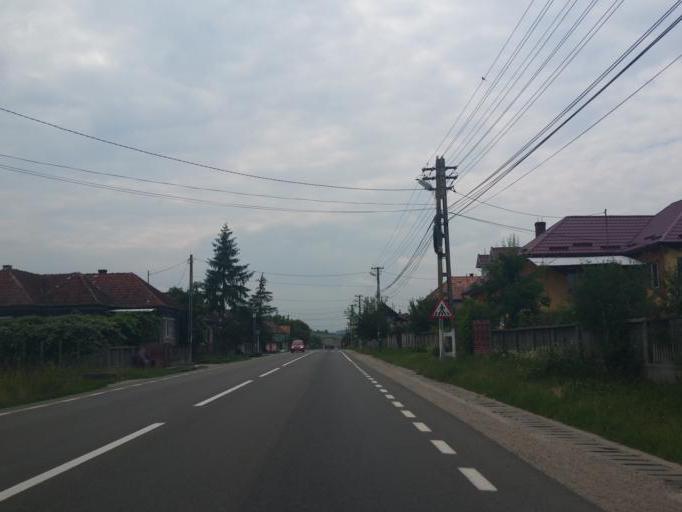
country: RO
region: Salaj
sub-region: Comuna Hida
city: Hida
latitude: 47.0459
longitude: 23.2508
